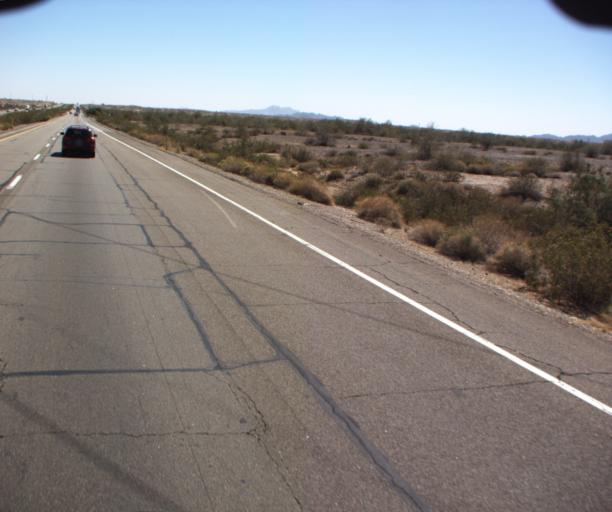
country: US
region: Arizona
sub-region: Yuma County
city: Wellton
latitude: 32.6655
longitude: -114.2779
